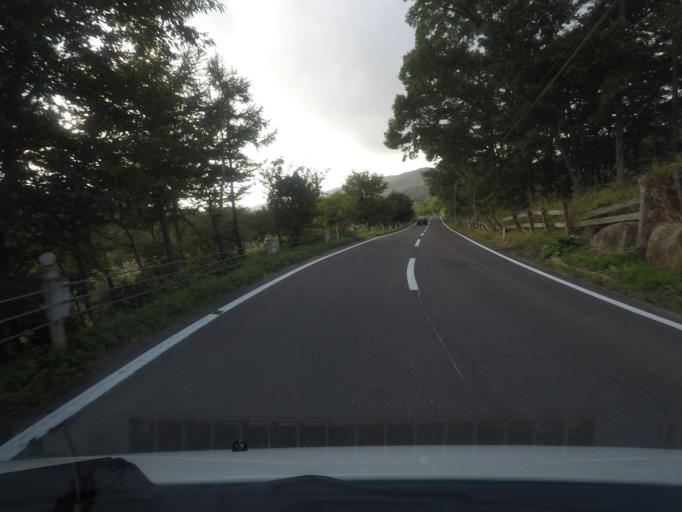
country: JP
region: Fukushima
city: Funehikimachi-funehiki
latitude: 37.5853
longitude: 140.7161
